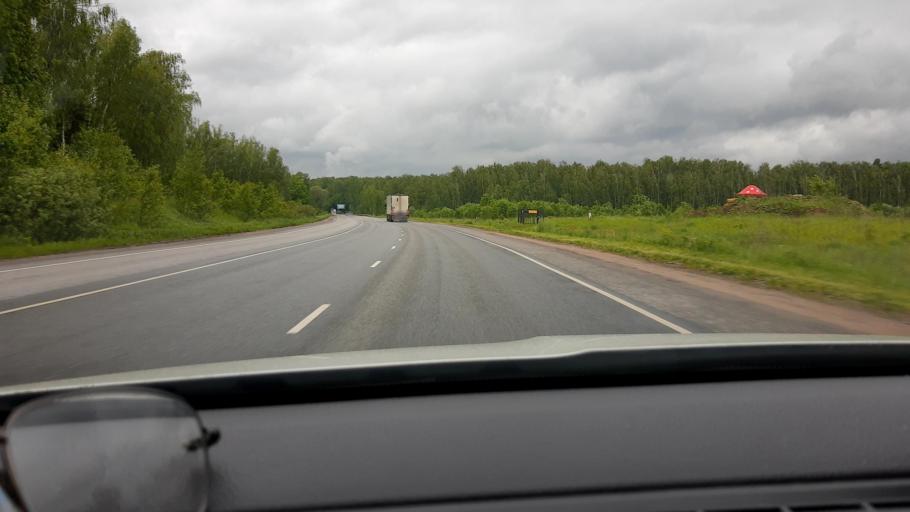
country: RU
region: Moskovskaya
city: Gorki-Leninskiye
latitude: 55.5239
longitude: 37.7902
